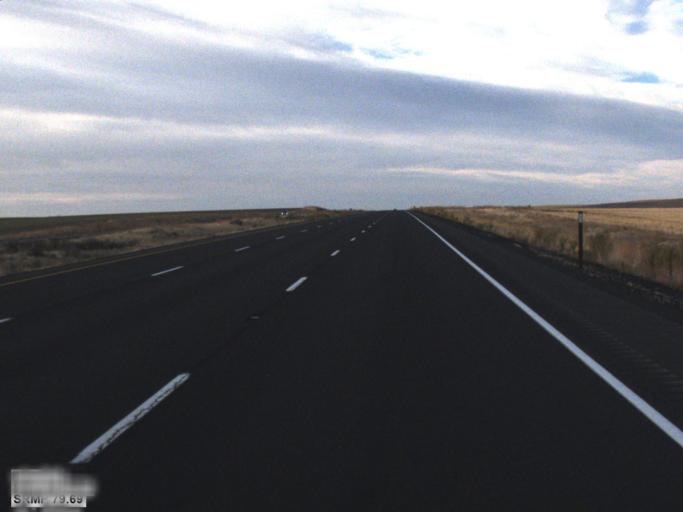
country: US
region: Washington
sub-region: Adams County
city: Ritzville
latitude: 46.9367
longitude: -118.5864
